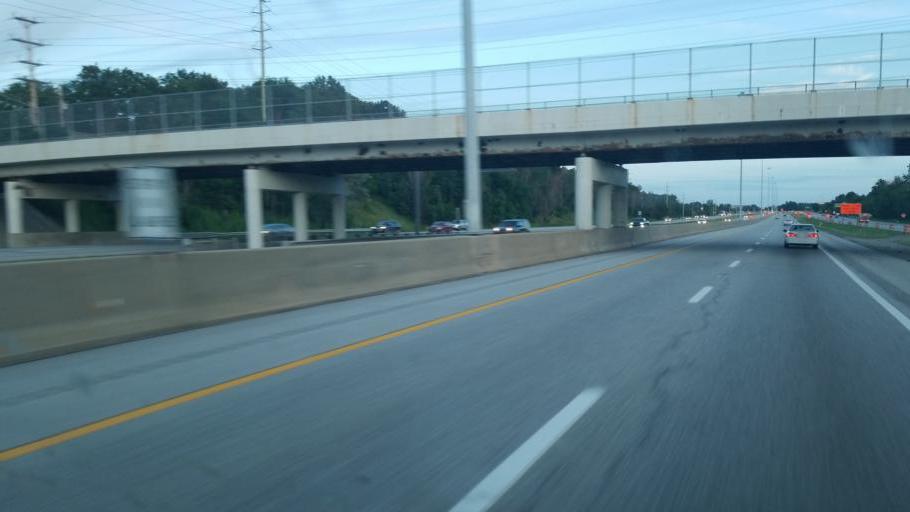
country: US
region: Ohio
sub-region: Cuyahoga County
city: Mayfield
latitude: 41.5529
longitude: -81.4484
